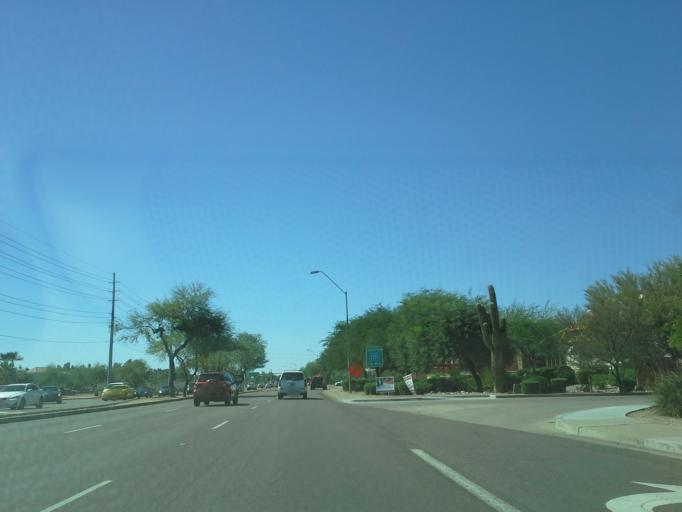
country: US
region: Arizona
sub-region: Maricopa County
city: Scottsdale
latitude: 33.5827
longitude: -111.8865
